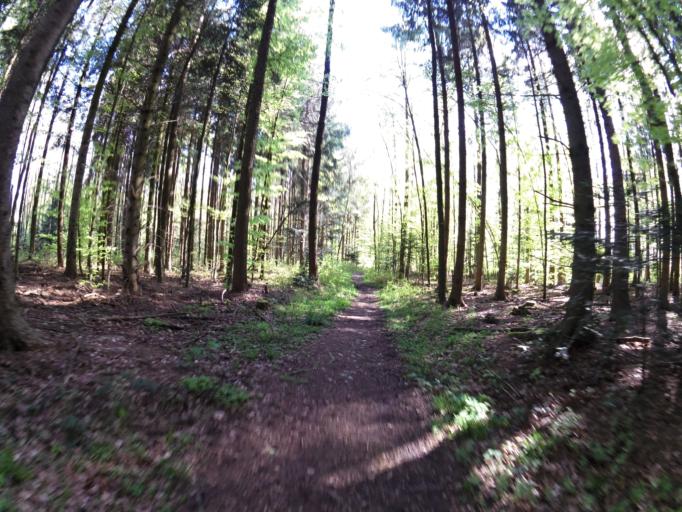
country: CH
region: Solothurn
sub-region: Bezirk Goesgen
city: Niedererlinsbach
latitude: 47.4040
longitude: 8.0242
